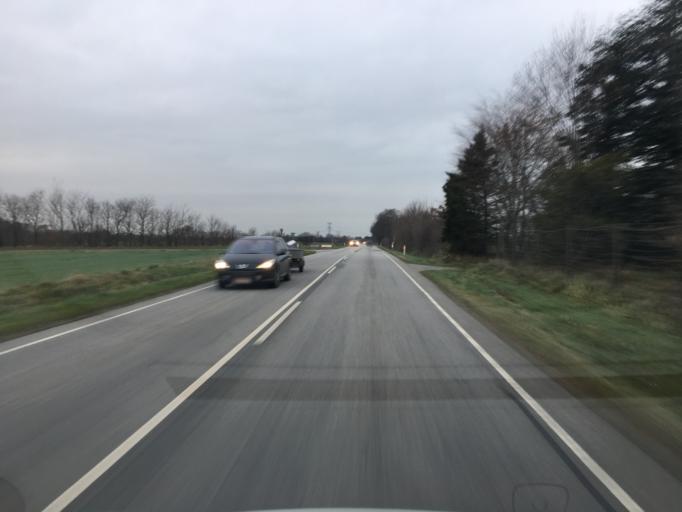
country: DK
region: South Denmark
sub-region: Aabenraa Kommune
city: Tinglev
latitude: 54.9971
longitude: 9.2319
